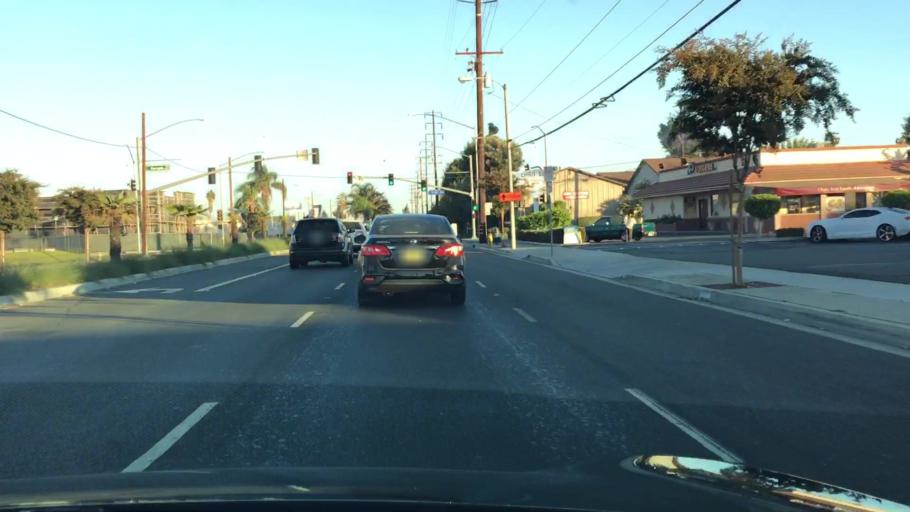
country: US
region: California
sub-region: Los Angeles County
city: Santa Fe Springs
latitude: 33.9589
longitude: -118.1072
